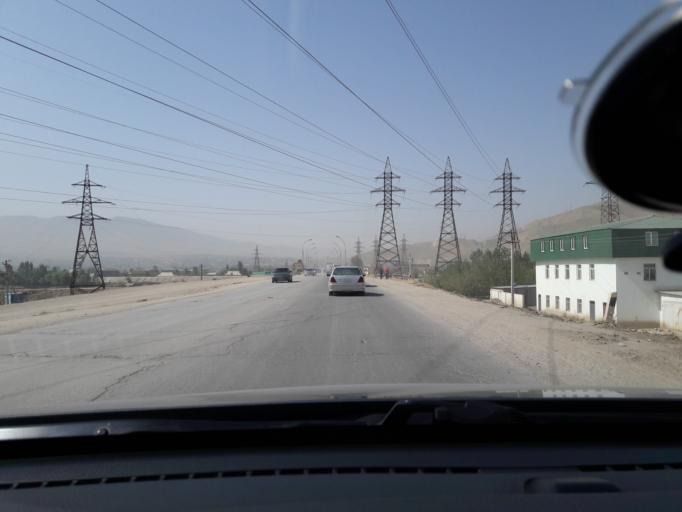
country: TJ
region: Dushanbe
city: Boshkengash
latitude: 38.4608
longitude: 68.7371
